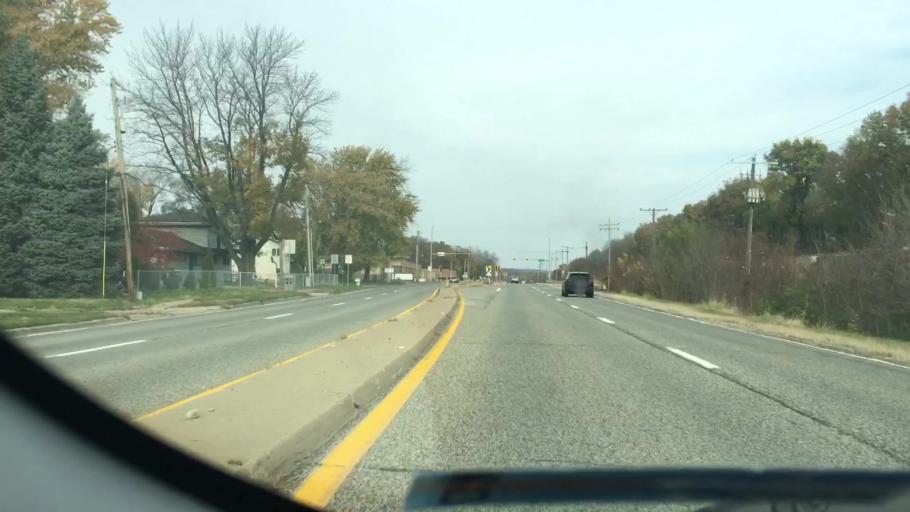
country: US
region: Illinois
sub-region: Peoria County
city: Peoria Heights
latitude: 40.7568
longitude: -89.5639
